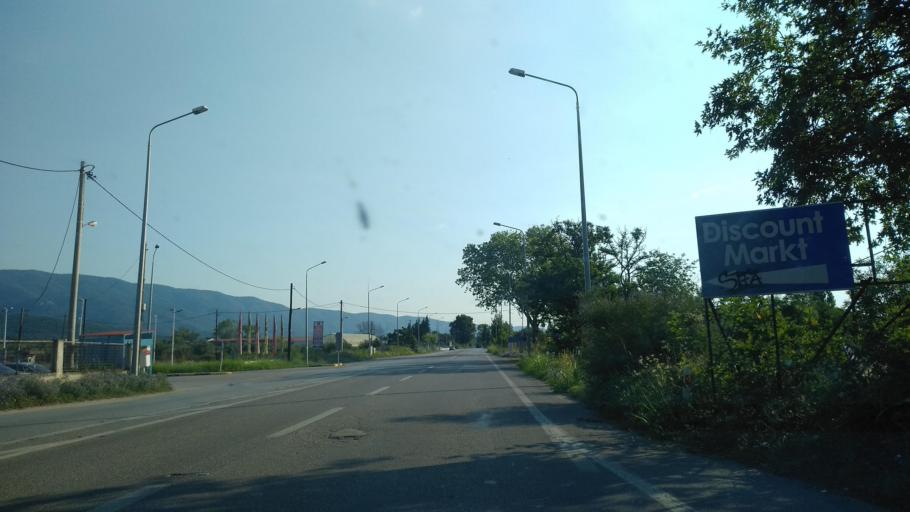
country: GR
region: Central Macedonia
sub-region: Nomos Thessalonikis
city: Nea Vrasna
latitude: 40.6896
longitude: 23.6819
